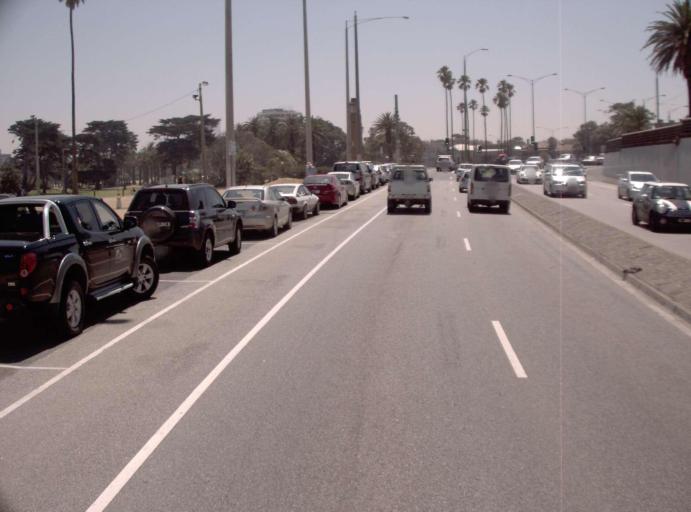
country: AU
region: Victoria
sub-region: Port Phillip
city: St Kilda West
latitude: -37.8638
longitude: 144.9721
